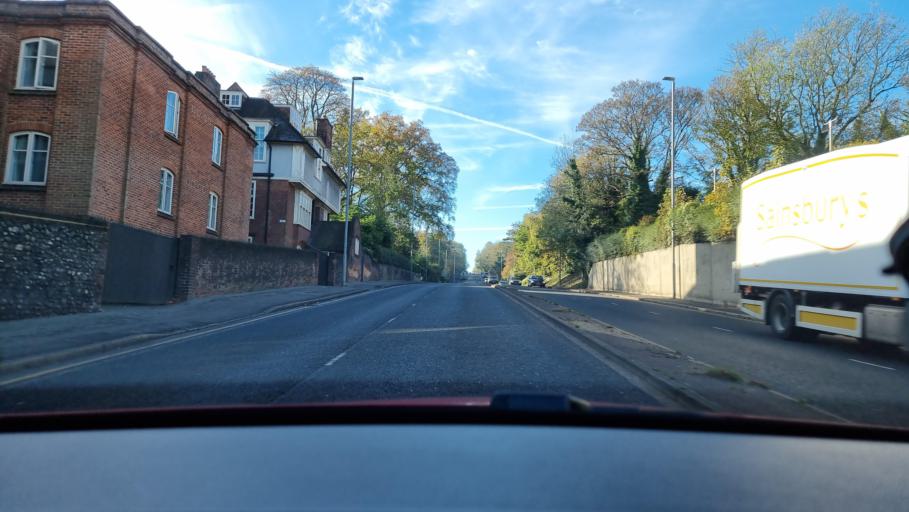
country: GB
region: England
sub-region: Buckinghamshire
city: High Wycombe
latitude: 51.6250
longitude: -0.7534
